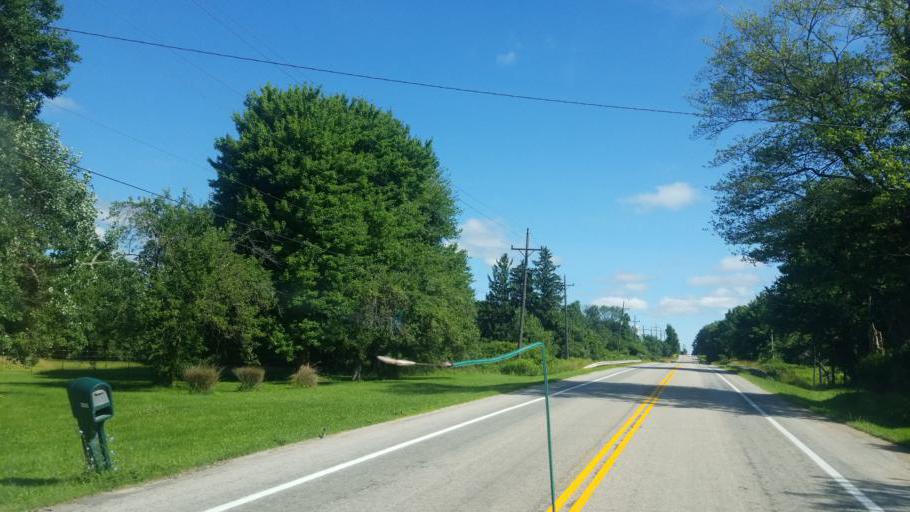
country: US
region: Ohio
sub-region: Ashtabula County
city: Conneaut
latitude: 41.7957
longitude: -80.5719
